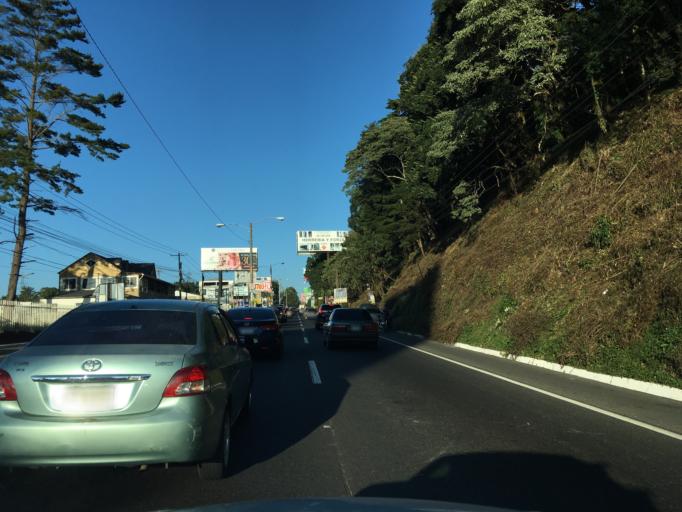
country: GT
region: Guatemala
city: Santa Catarina Pinula
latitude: 14.5341
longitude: -90.4600
